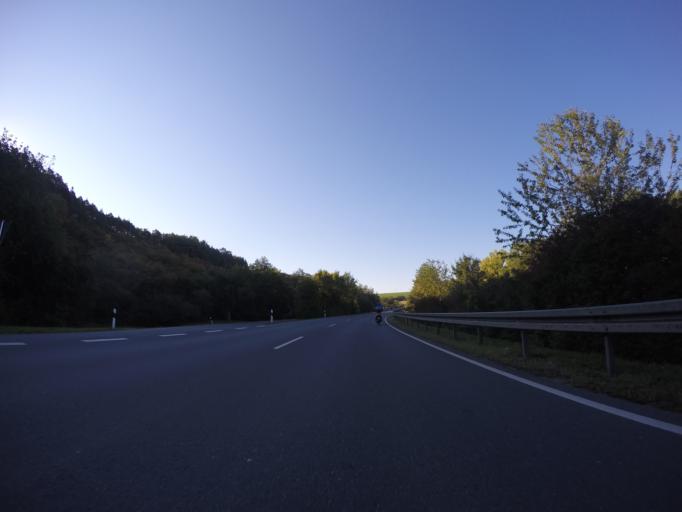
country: DE
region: Bavaria
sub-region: Regierungsbezirk Unterfranken
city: Marktheidenfeld
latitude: 49.8329
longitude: 9.6113
